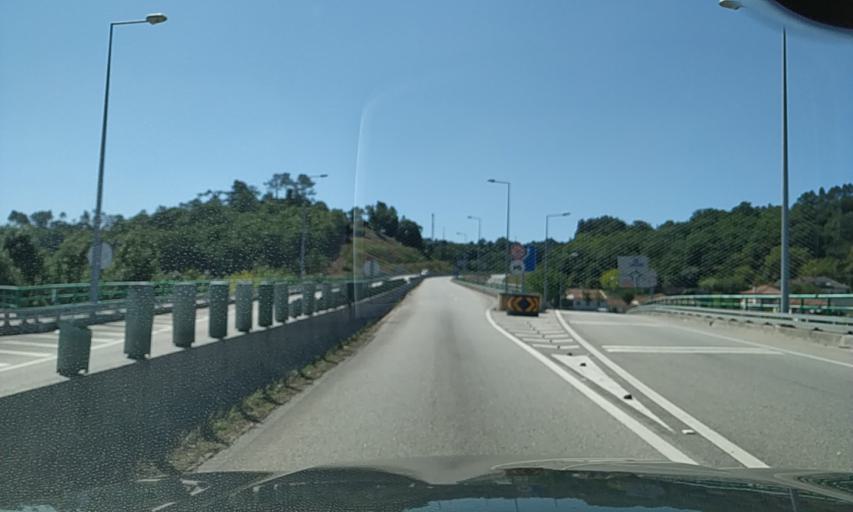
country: PT
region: Aveiro
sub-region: Agueda
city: Agueda
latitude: 40.5676
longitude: -8.4487
